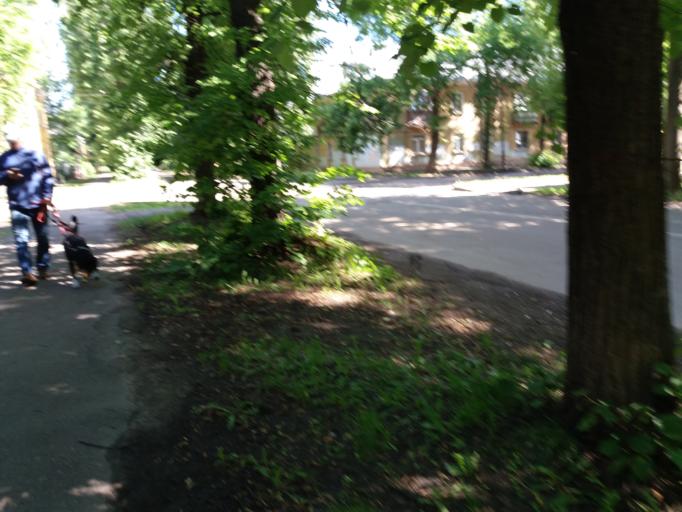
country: RU
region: Jaroslavl
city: Yaroslavl
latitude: 57.6404
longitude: 39.8348
